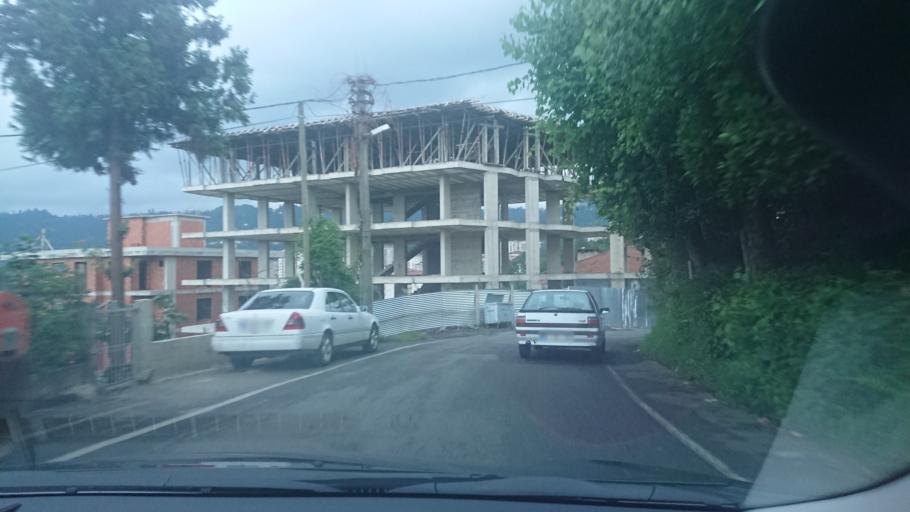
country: TR
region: Rize
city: Rize
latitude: 41.0278
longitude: 40.5118
